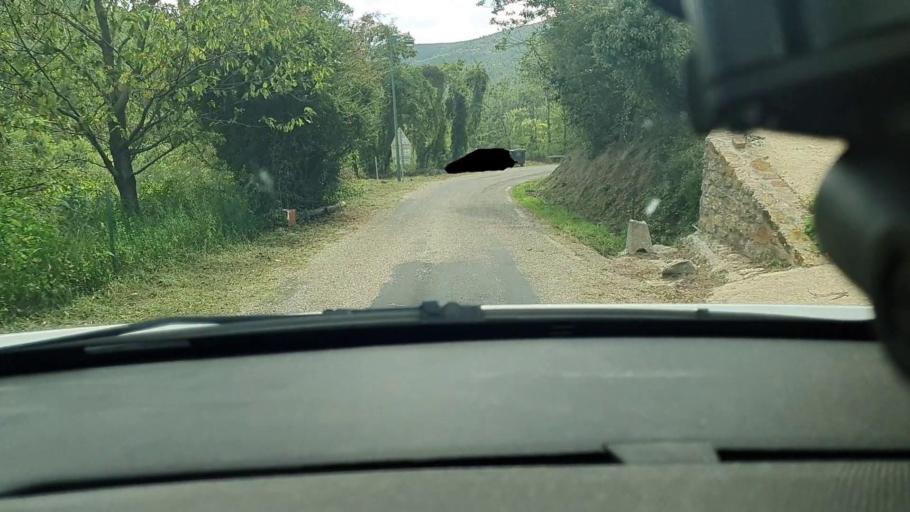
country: FR
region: Languedoc-Roussillon
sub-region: Departement du Gard
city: Branoux-les-Taillades
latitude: 44.2928
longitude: 4.0088
